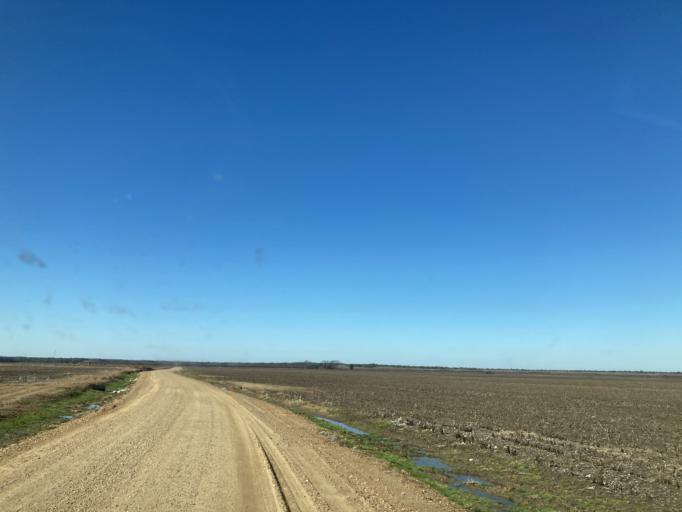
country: US
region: Mississippi
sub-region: Sharkey County
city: Rolling Fork
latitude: 32.8228
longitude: -90.7312
